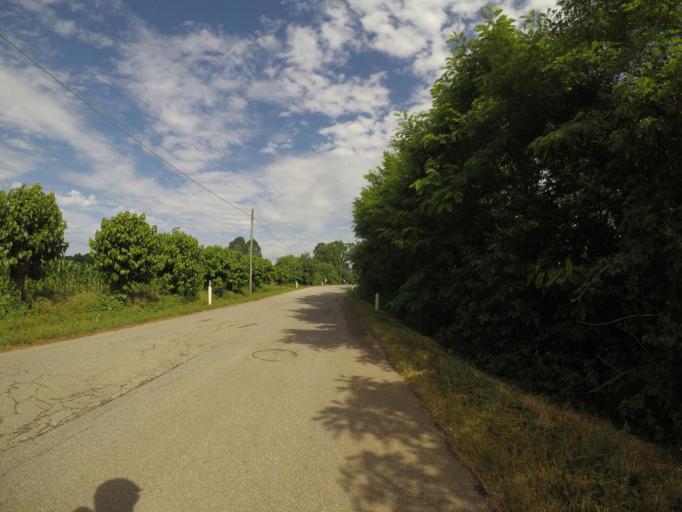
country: IT
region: Friuli Venezia Giulia
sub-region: Provincia di Udine
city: Lestizza
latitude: 45.9605
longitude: 13.1286
